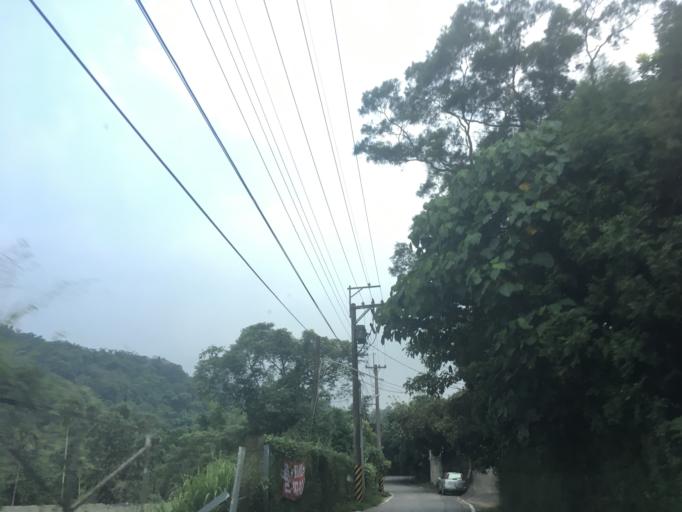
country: TW
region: Taiwan
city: Fengyuan
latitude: 24.1887
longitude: 120.7472
